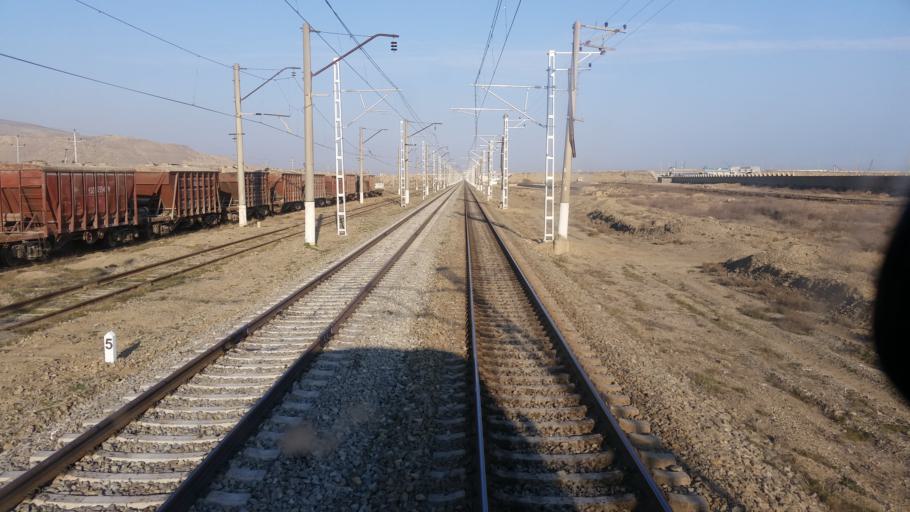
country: AZ
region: Baki
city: Korgoz
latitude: 40.2489
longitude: 49.6104
